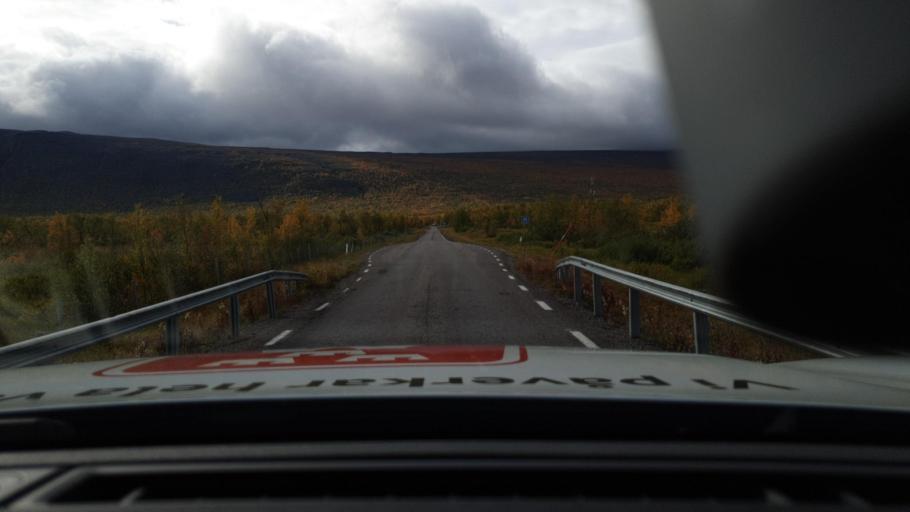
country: SE
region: Norrbotten
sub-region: Kiruna Kommun
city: Kiruna
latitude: 67.8554
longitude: 19.0214
